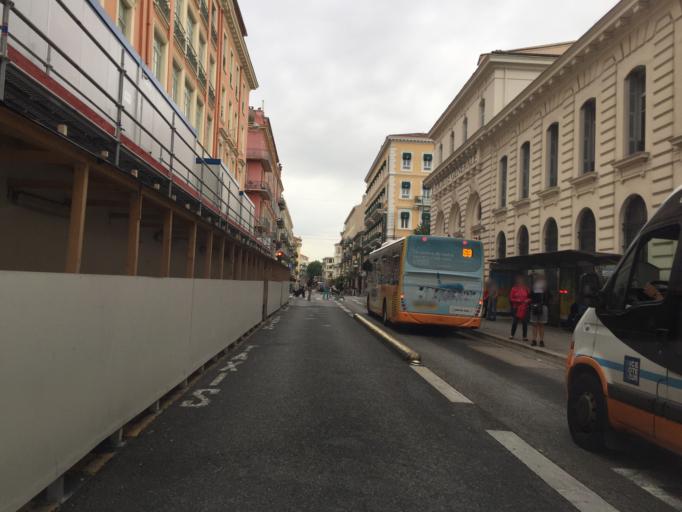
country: FR
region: Provence-Alpes-Cote d'Azur
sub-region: Departement des Alpes-Maritimes
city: Nice
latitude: 43.6990
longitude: 7.2699
